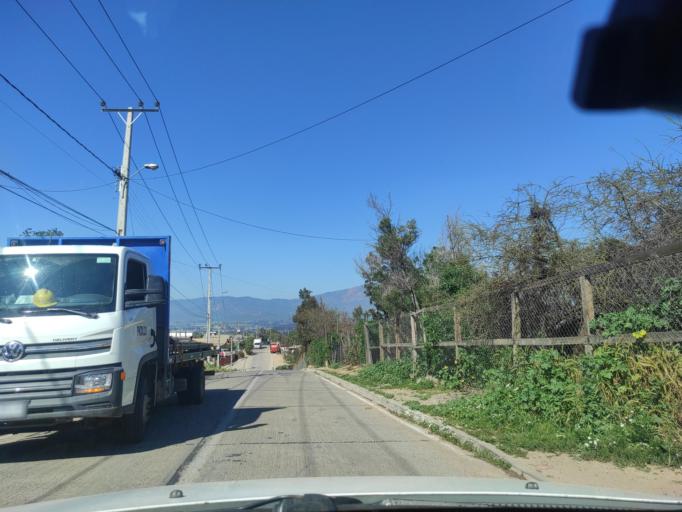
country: CL
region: Valparaiso
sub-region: Provincia de Marga Marga
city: Limache
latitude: -32.9877
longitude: -71.2249
